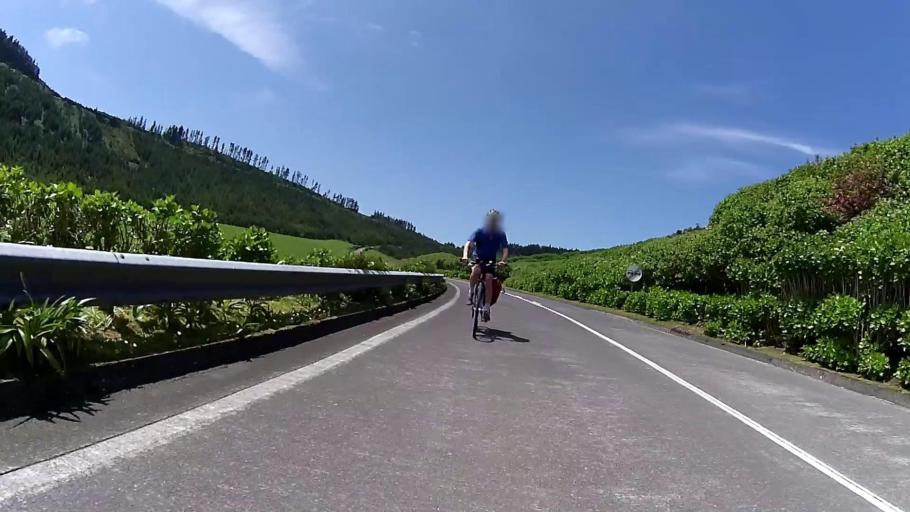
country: PT
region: Azores
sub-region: Ponta Delgada
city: Arrifes
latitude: 37.8411
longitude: -25.7781
